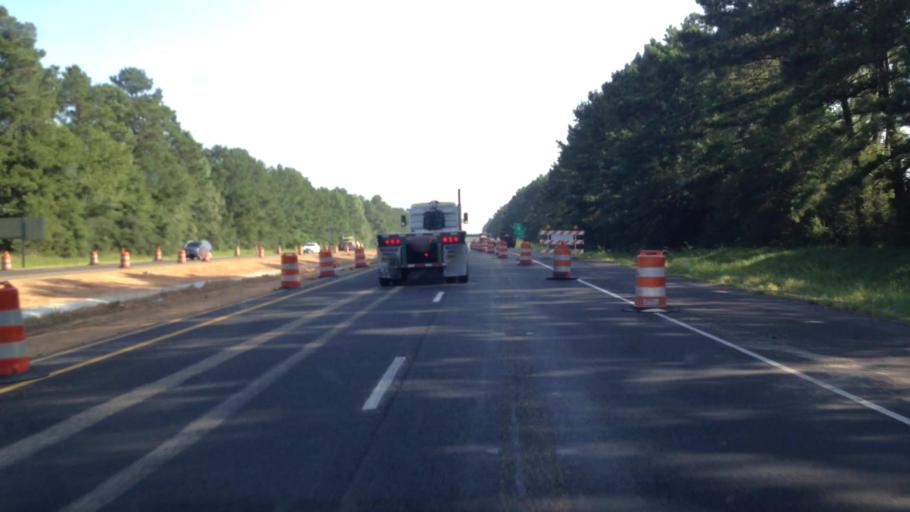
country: US
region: Mississippi
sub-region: Pike County
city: McComb
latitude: 31.2000
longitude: -90.4840
